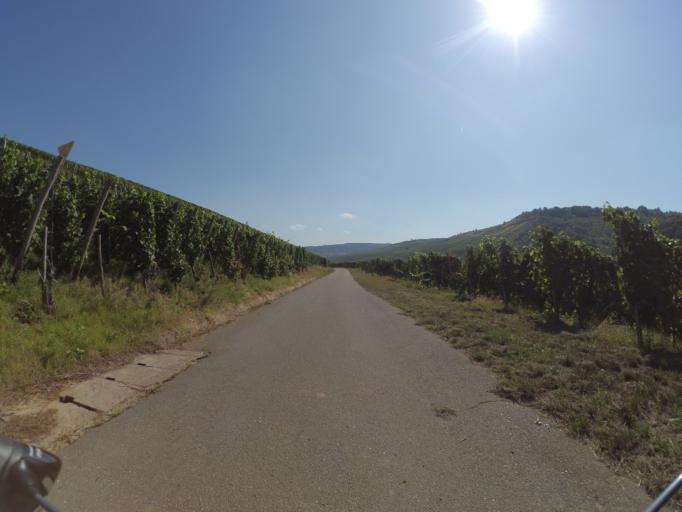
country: DE
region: Rheinland-Pfalz
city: Neumagen-Dhron
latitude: 49.8464
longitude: 6.8954
